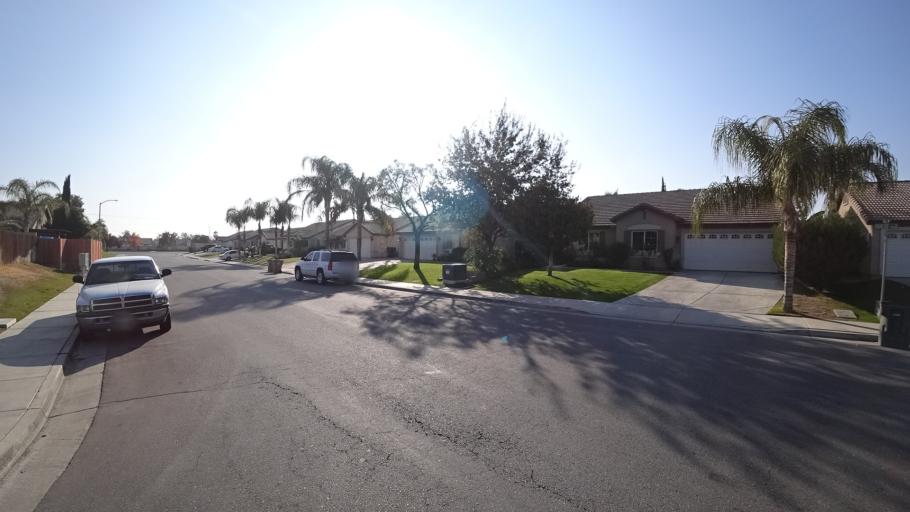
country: US
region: California
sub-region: Kern County
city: Greenfield
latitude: 35.2826
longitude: -119.0159
